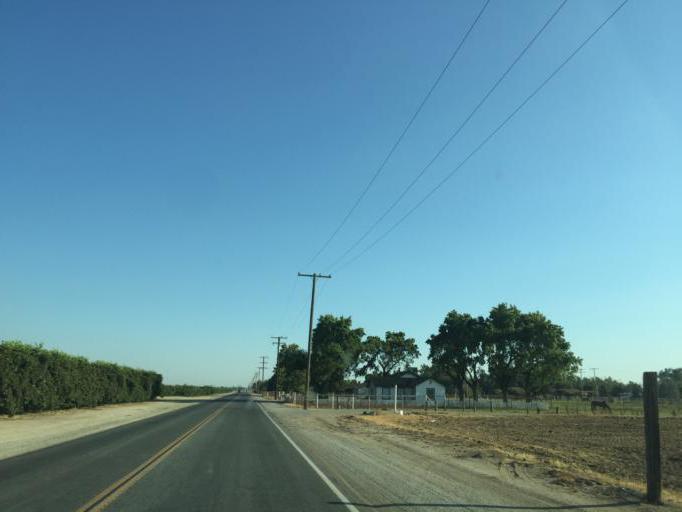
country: US
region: California
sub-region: Tulare County
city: Ivanhoe
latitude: 36.4263
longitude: -119.2780
